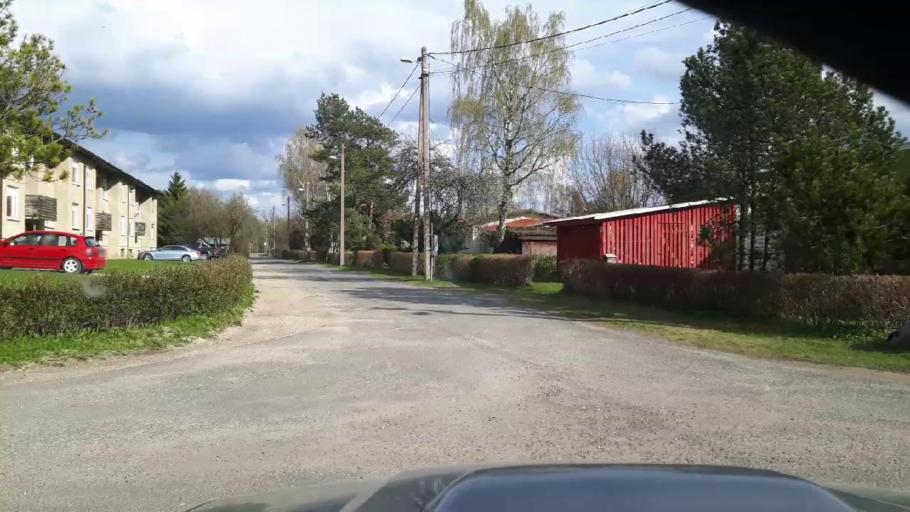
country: EE
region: Paernumaa
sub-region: Tootsi vald
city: Tootsi
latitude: 58.5159
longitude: 24.8146
